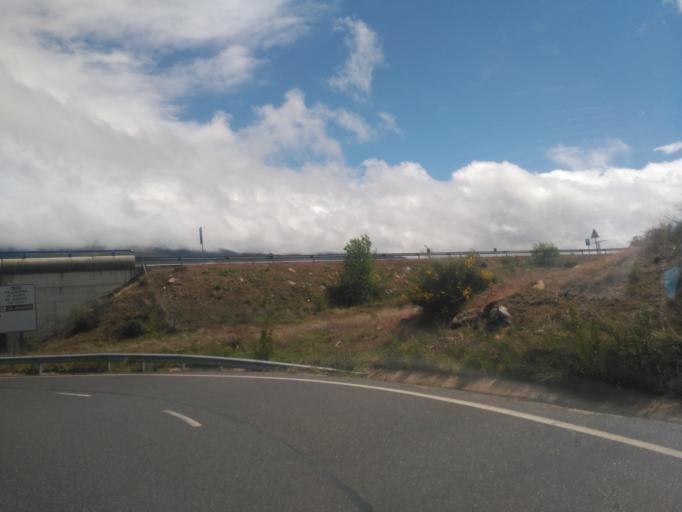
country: ES
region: Castille and Leon
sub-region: Provincia de Salamanca
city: Vallejera de Riofrio
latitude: 40.4117
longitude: -5.7211
